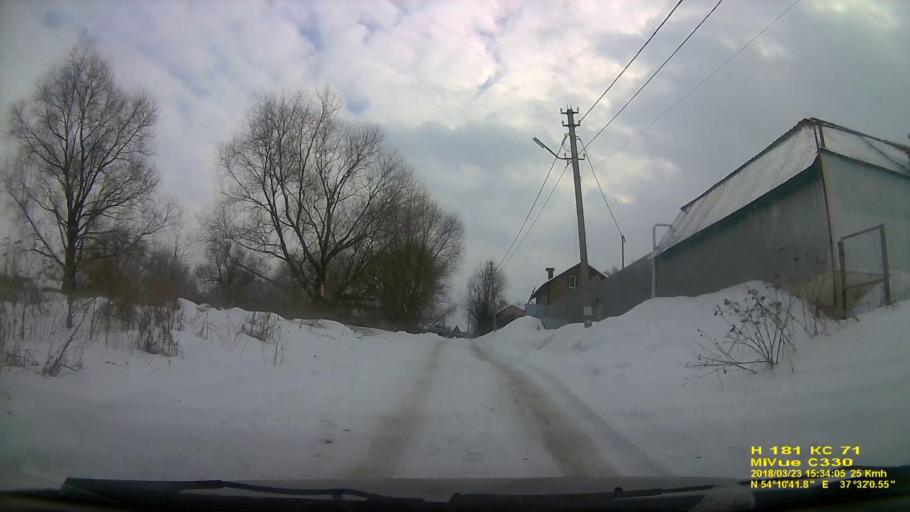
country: RU
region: Tula
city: Kosaya Gora
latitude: 54.1782
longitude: 37.5335
